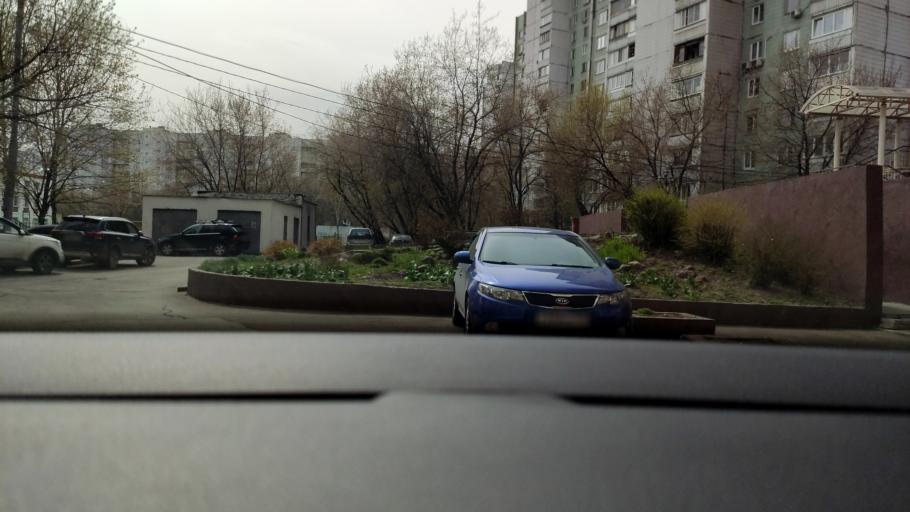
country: RU
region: Moscow
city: Leonovo
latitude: 55.8756
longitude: 37.6618
